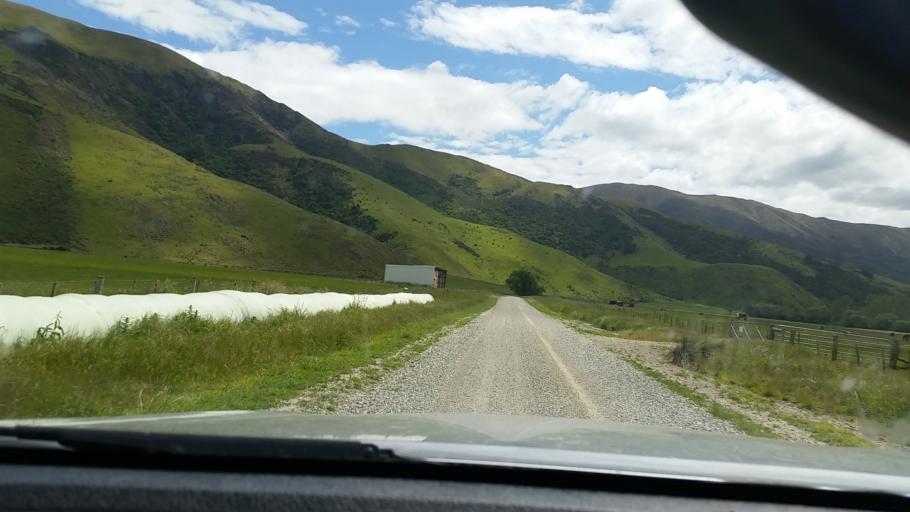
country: NZ
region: Otago
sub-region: Queenstown-Lakes District
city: Kingston
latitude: -45.6899
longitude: 168.6350
